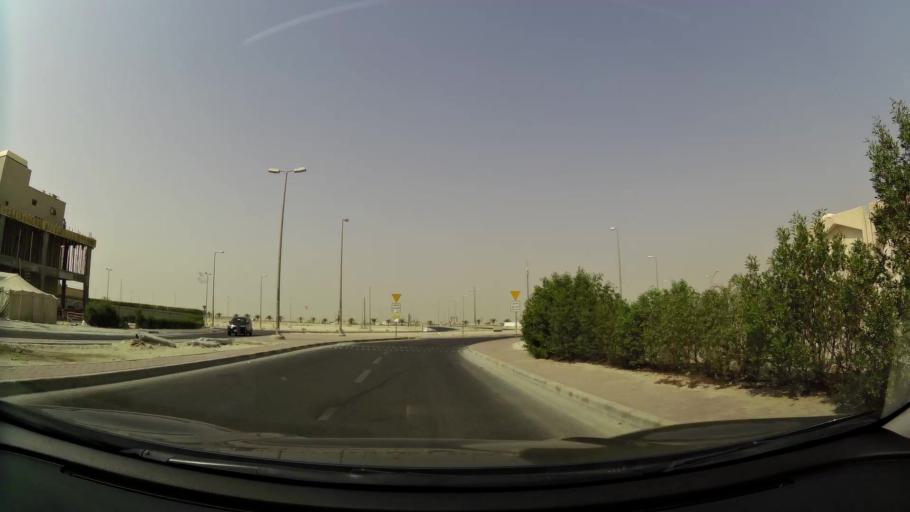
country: KW
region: Muhafazat al Jahra'
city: Al Jahra'
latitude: 29.3231
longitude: 47.7192
